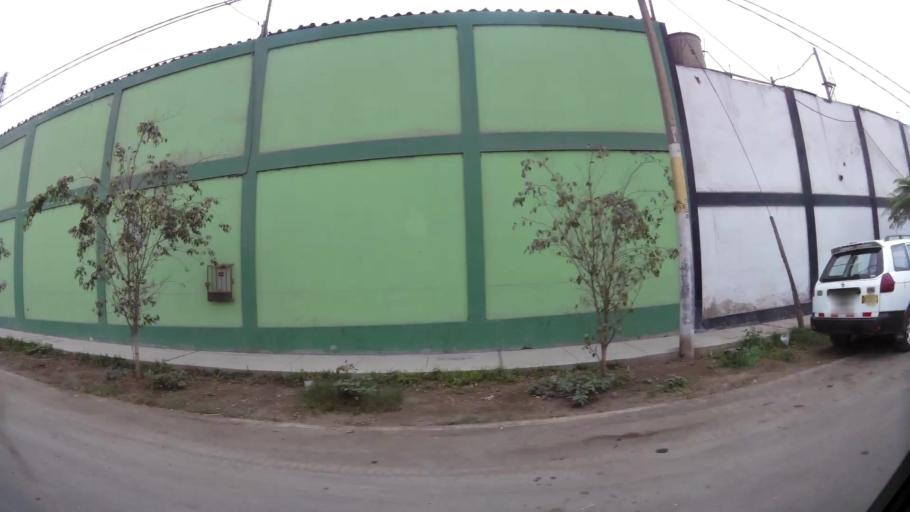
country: PE
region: Lima
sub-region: Lima
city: Urb. Santo Domingo
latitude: -11.8780
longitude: -77.0678
